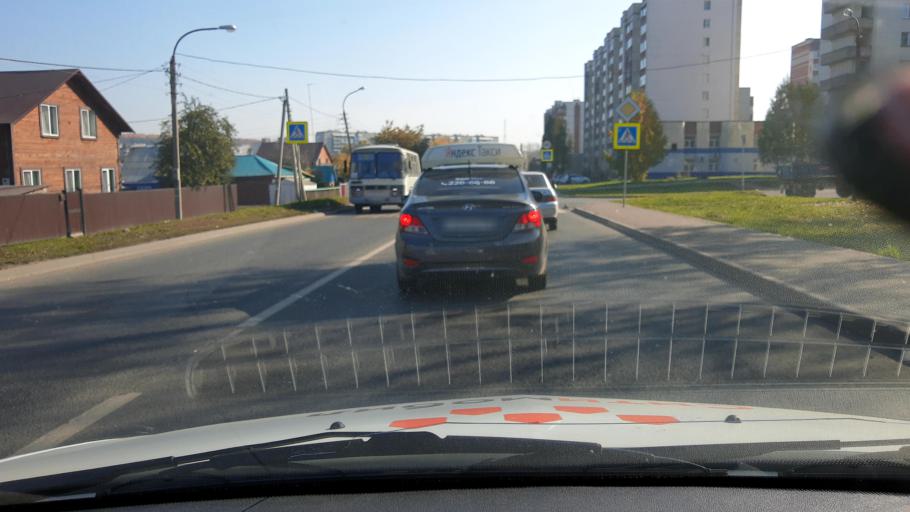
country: RU
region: Bashkortostan
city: Ufa
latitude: 54.8215
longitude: 56.1157
